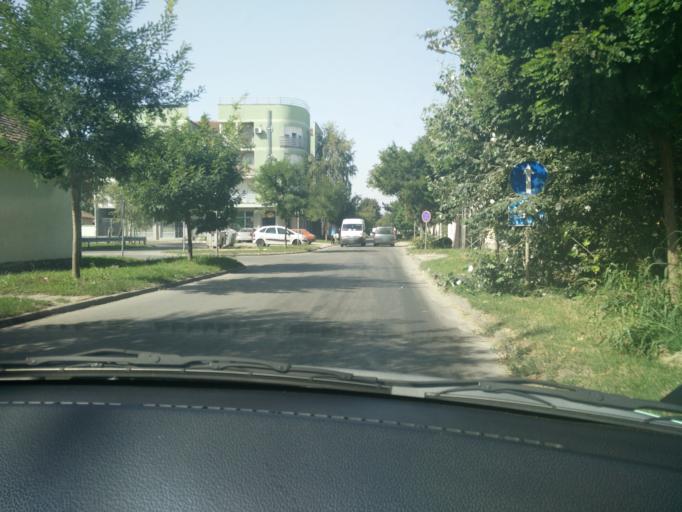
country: RS
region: Autonomna Pokrajina Vojvodina
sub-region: Juznobacki Okrug
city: Novi Sad
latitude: 45.2639
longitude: 19.8513
